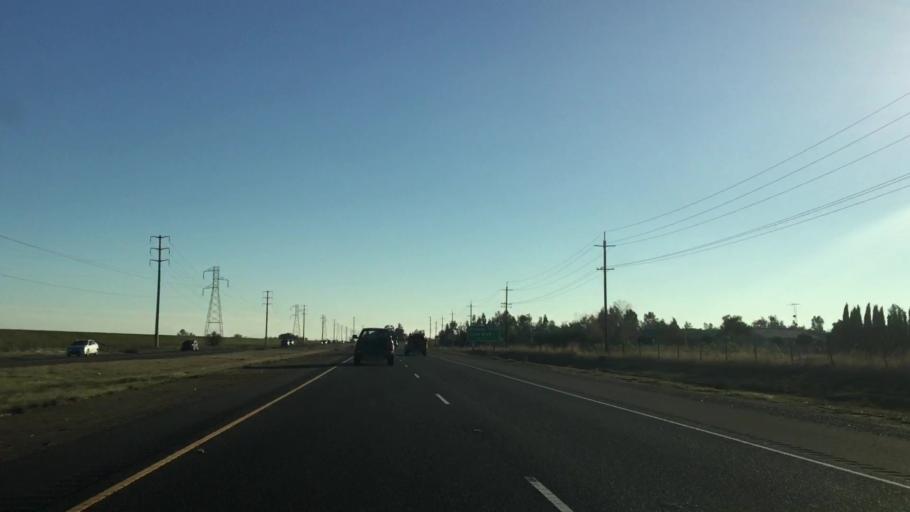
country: US
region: California
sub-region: Yuba County
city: Plumas Lake
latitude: 39.0407
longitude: -121.5433
